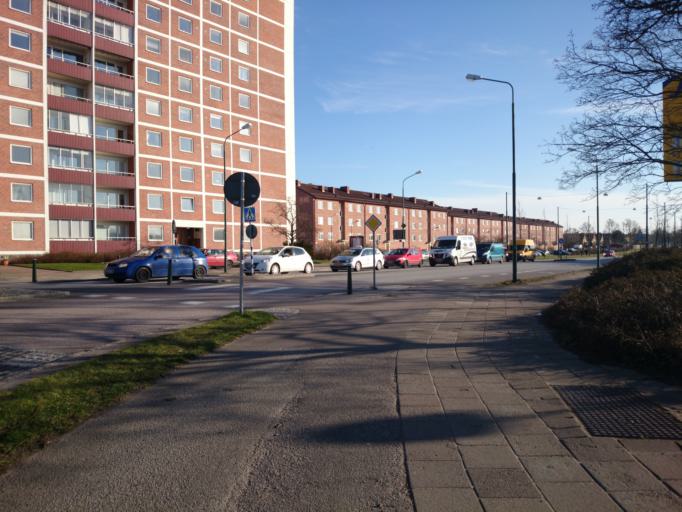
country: SE
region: Skane
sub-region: Malmo
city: Malmoe
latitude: 55.6007
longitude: 13.0393
